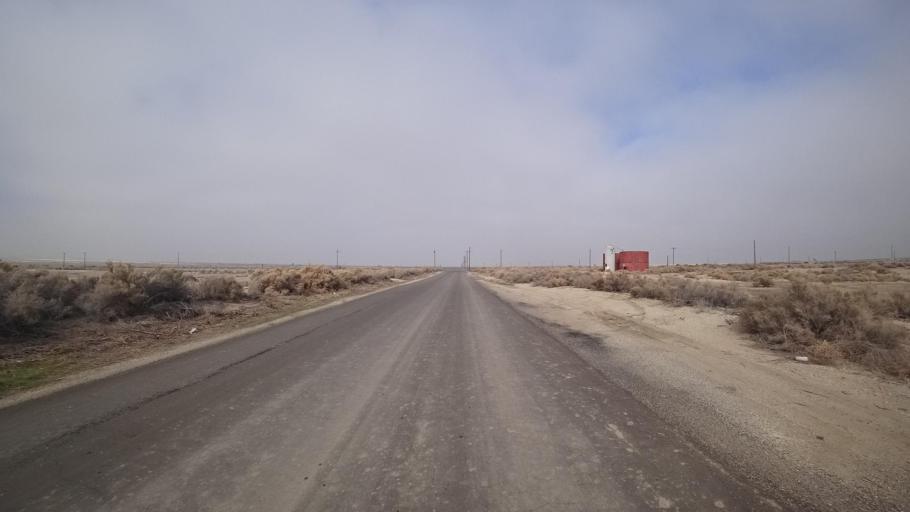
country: US
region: California
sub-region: Kern County
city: Maricopa
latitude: 35.0562
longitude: -119.3671
